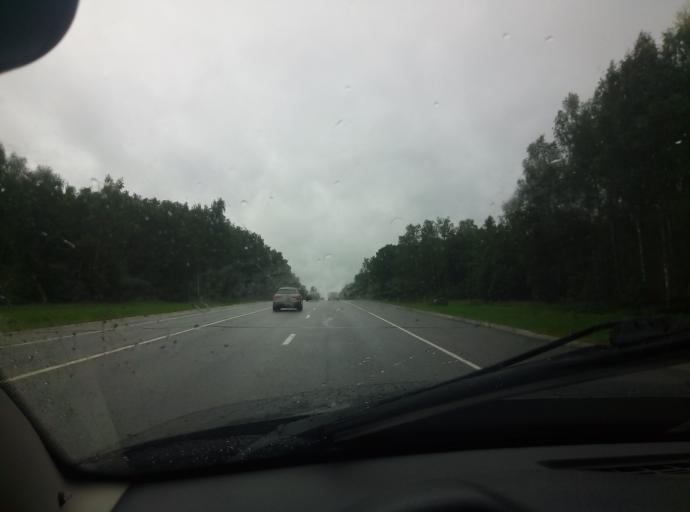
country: RU
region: Tula
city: Leninskiy
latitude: 54.3888
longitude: 37.5109
